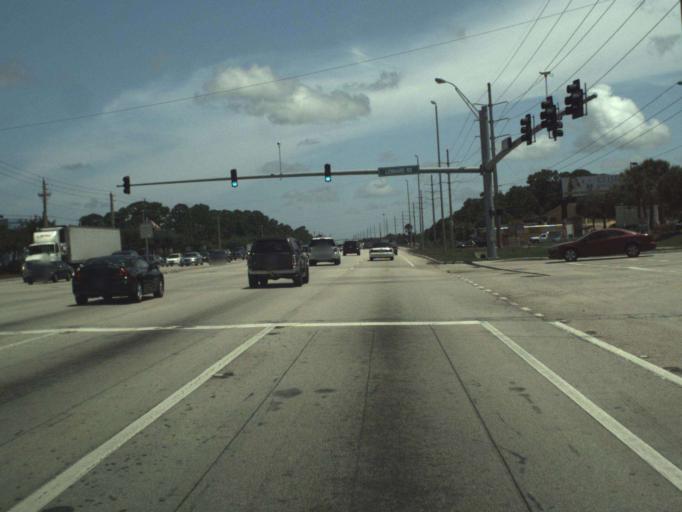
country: US
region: Florida
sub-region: Martin County
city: North River Shores
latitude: 27.2658
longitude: -80.2855
